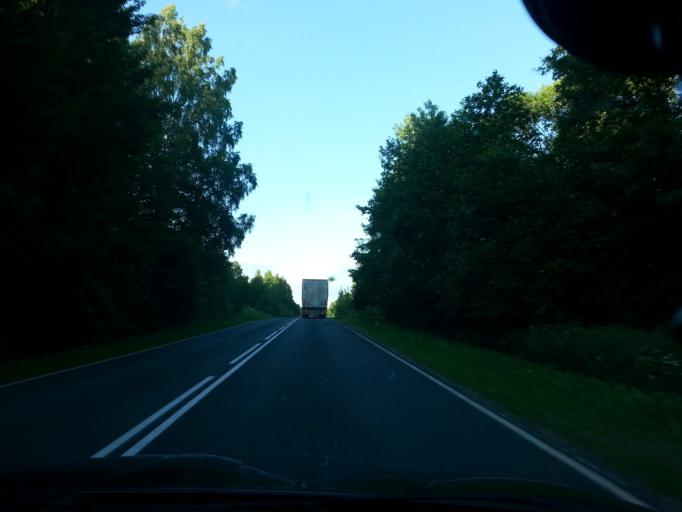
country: BY
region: Minsk
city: Svir
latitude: 54.8743
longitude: 26.3562
